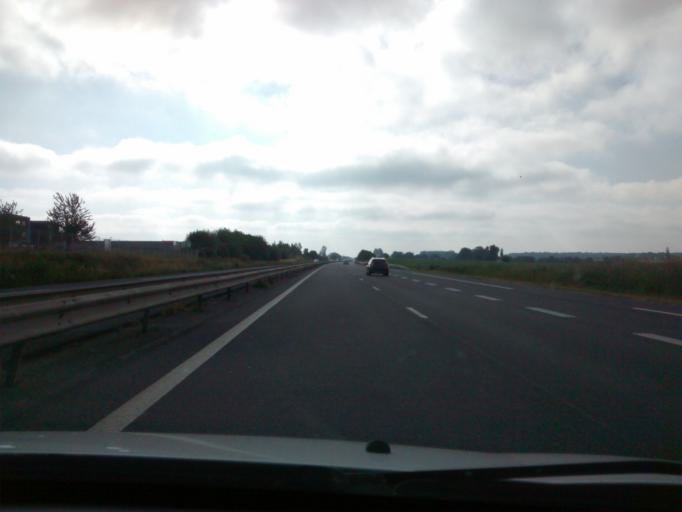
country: FR
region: Brittany
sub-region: Departement d'Ille-et-Vilaine
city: Torce
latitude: 48.0749
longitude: -1.2631
